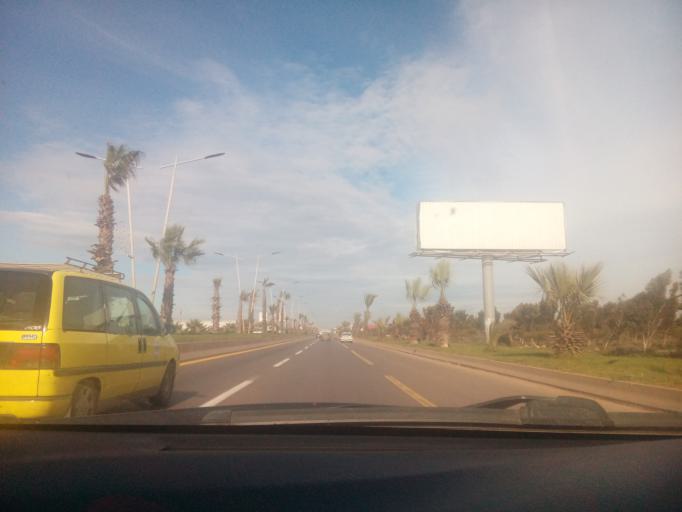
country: DZ
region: Oran
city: Es Senia
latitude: 35.6311
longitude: -0.5869
